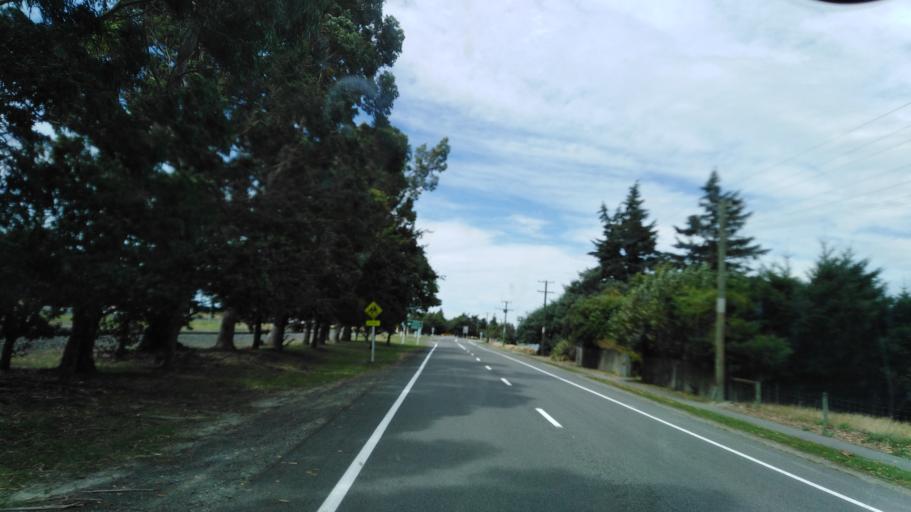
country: NZ
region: Canterbury
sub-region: Selwyn District
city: Darfield
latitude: -43.3909
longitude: 172.0230
